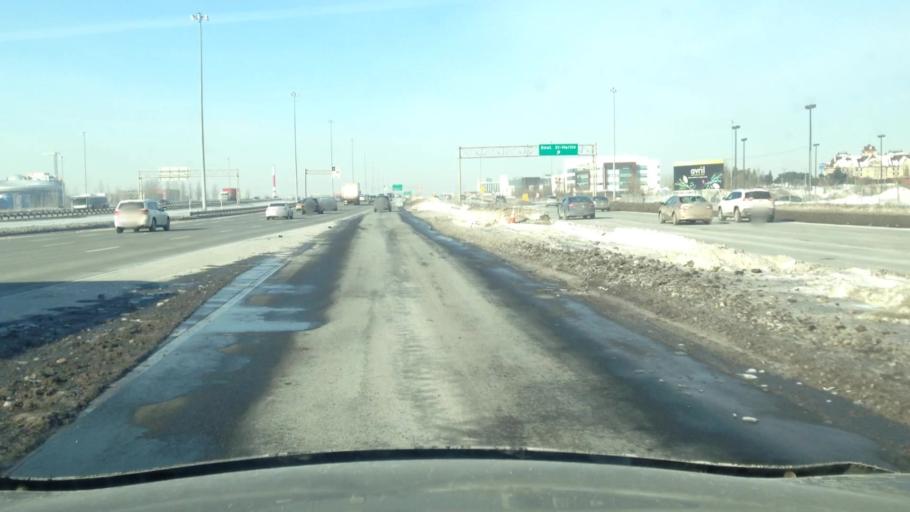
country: CA
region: Quebec
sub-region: Laval
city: Laval
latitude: 45.5599
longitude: -73.7335
